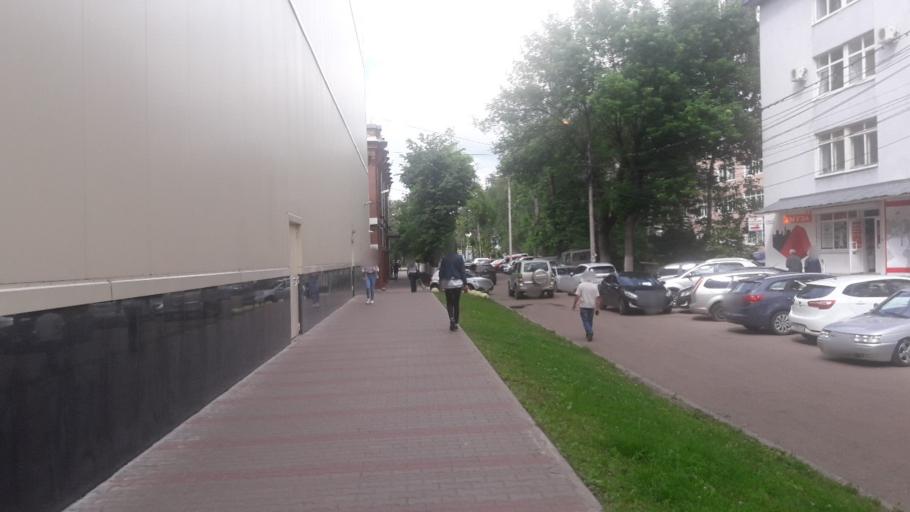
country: RU
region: Jaroslavl
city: Yaroslavl
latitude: 57.6265
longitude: 39.8729
